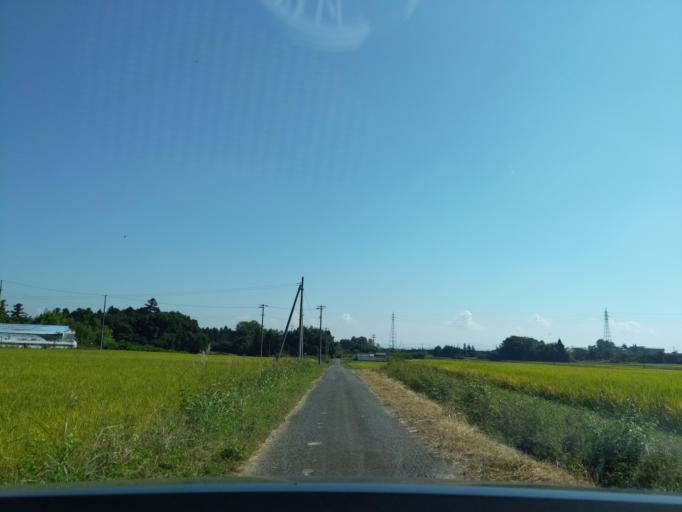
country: JP
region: Fukushima
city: Koriyama
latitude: 37.4129
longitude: 140.3190
